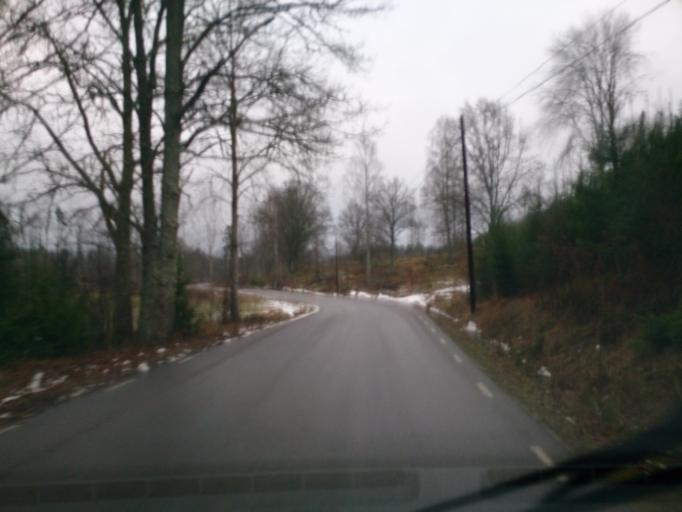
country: SE
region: OEstergoetland
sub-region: Atvidabergs Kommun
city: Atvidaberg
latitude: 58.2616
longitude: 16.1041
